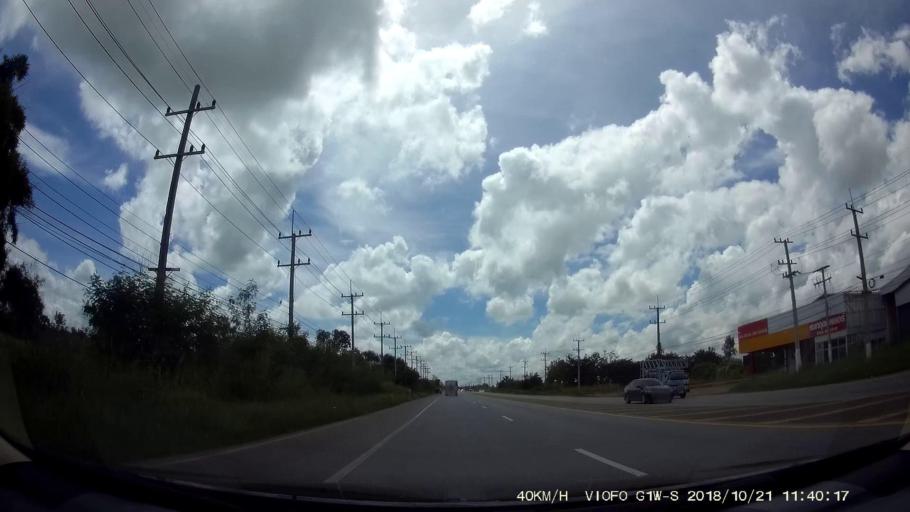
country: TH
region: Chaiyaphum
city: Chaiyaphum
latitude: 15.7145
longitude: 102.0159
